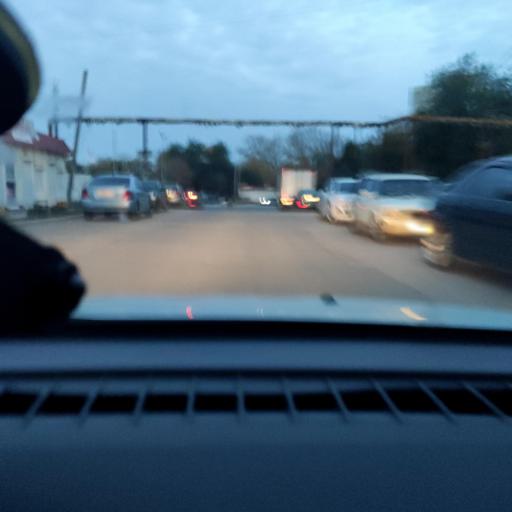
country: RU
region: Samara
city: Samara
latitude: 53.1072
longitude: 50.0811
